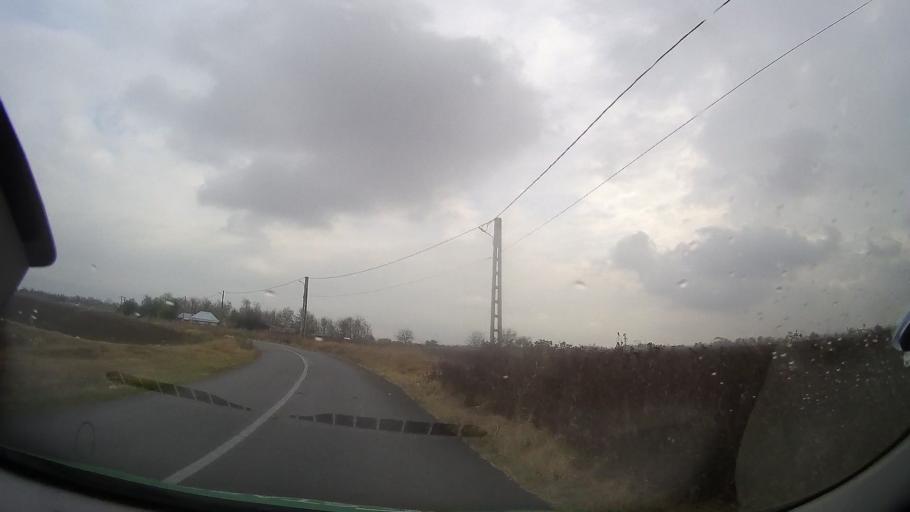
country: RO
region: Ialomita
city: Brazii
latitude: 44.7816
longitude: 26.3224
